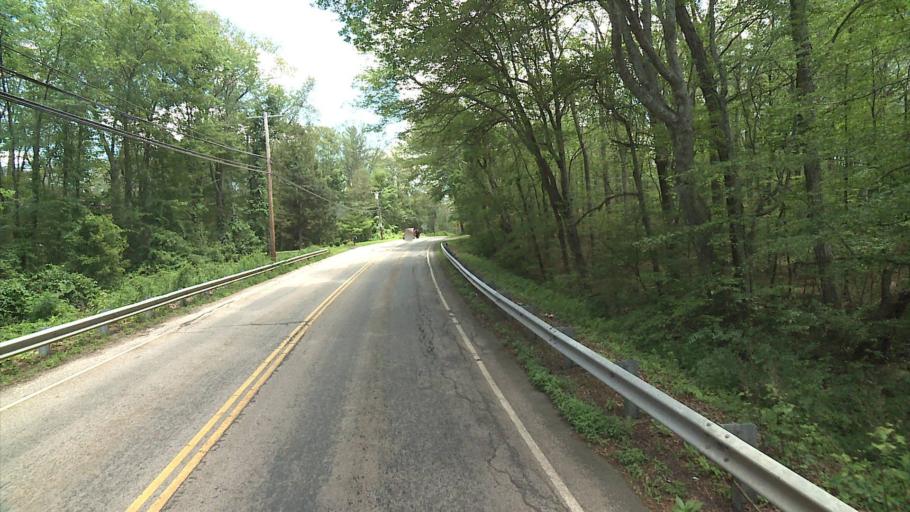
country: US
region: Connecticut
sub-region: Middlesex County
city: East Haddam
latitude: 41.4670
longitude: -72.4282
